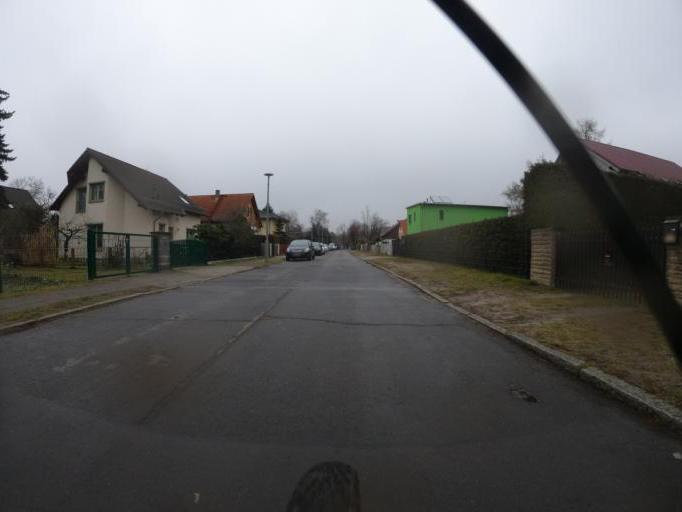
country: DE
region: Berlin
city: Biesdorf
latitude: 52.4851
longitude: 13.5581
